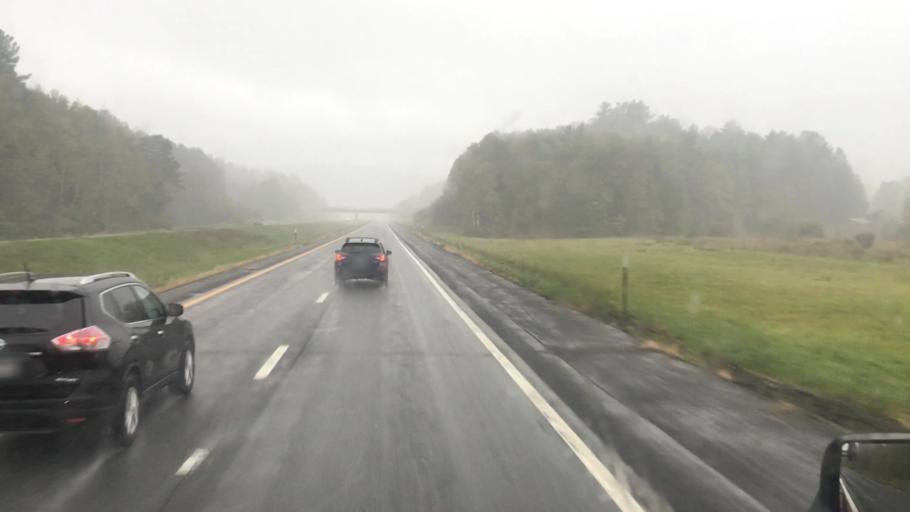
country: US
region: New York
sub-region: Chenango County
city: Bainbridge
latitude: 42.1848
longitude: -75.5992
